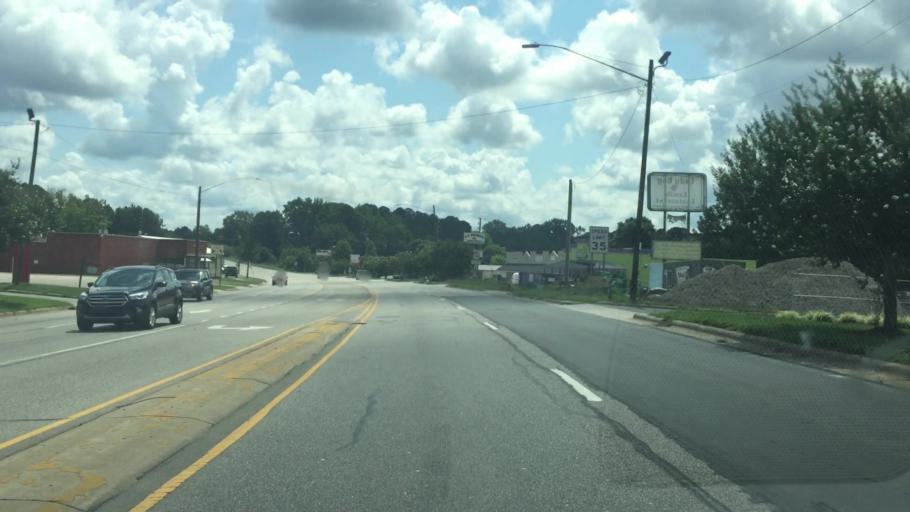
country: US
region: North Carolina
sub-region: Anson County
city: Wadesboro
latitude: 34.9634
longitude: -80.0564
